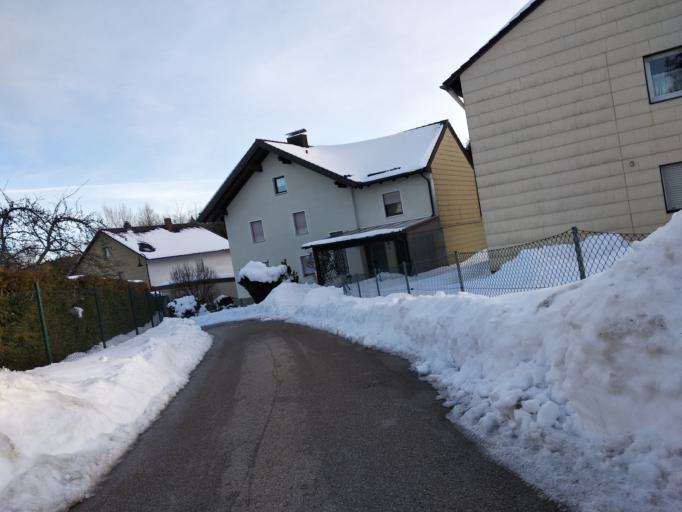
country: DE
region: Bavaria
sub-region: Upper Bavaria
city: Kirchseeon
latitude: 48.0715
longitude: 11.8791
